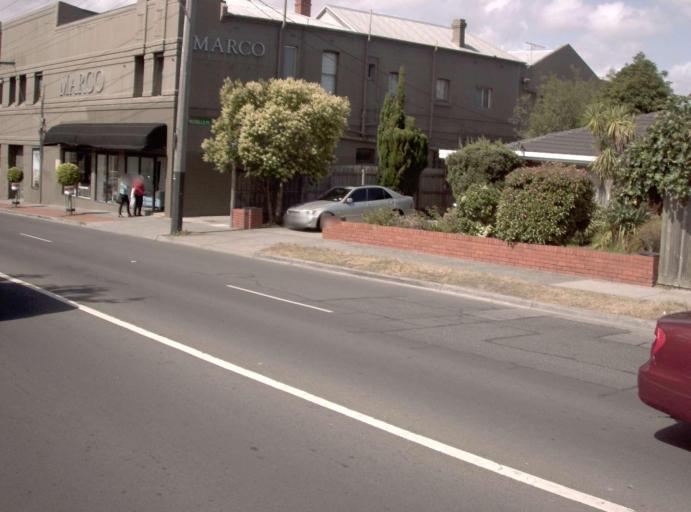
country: AU
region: Victoria
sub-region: Boroondara
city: Hawthorn East
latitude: -37.8246
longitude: 145.0446
